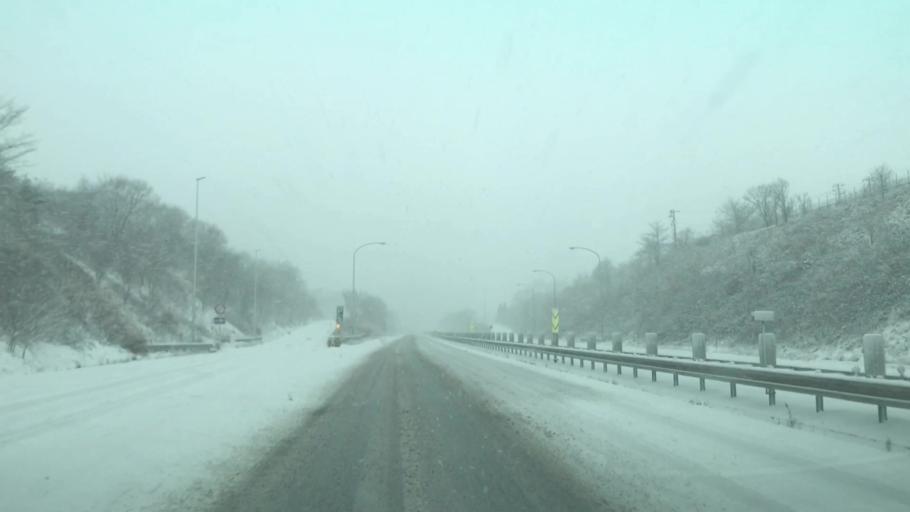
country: JP
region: Hokkaido
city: Muroran
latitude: 42.4453
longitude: 141.1517
